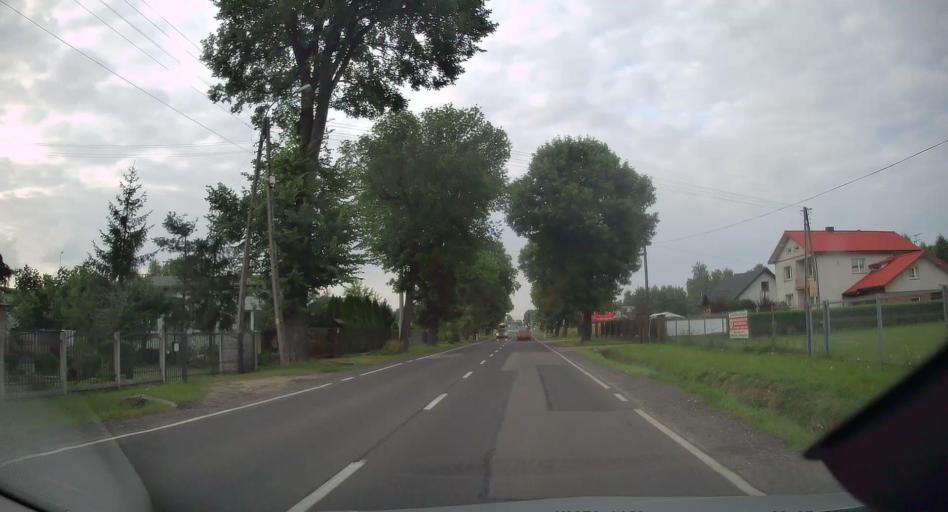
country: PL
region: Lodz Voivodeship
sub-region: Powiat radomszczanski
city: Radomsko
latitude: 51.1042
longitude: 19.4640
